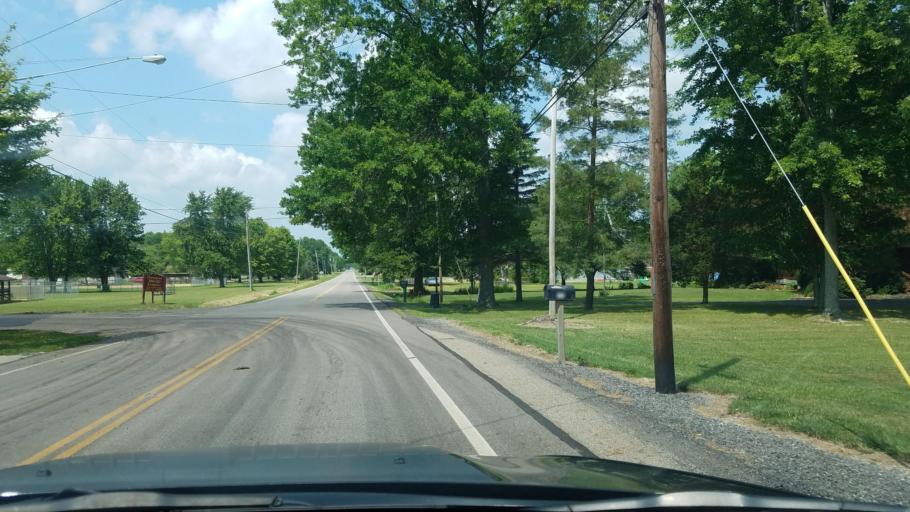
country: US
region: Ohio
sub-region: Trumbull County
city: Champion Heights
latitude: 41.3084
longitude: -80.8646
